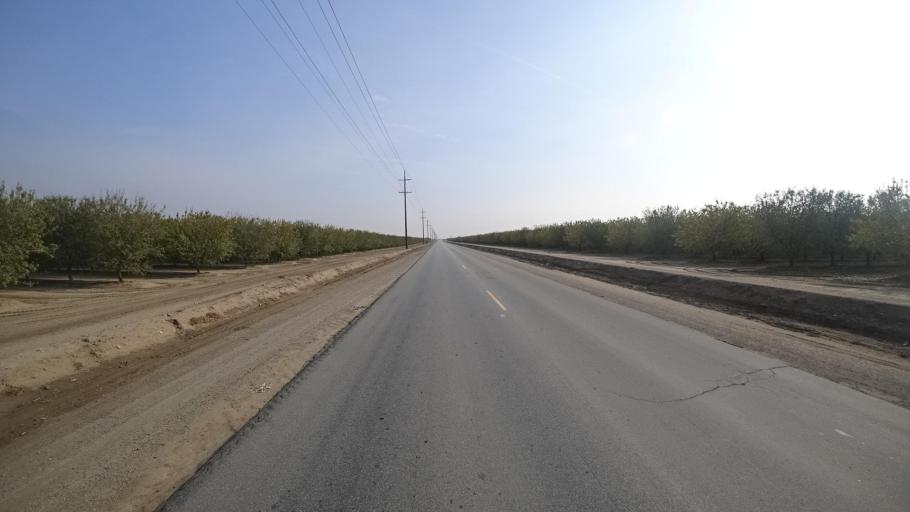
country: US
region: California
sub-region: Kern County
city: Weedpatch
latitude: 35.0953
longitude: -119.0027
